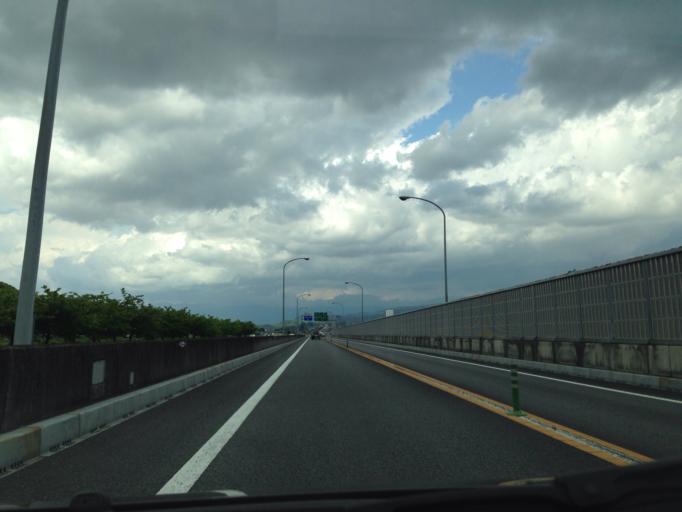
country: JP
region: Shizuoka
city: Mishima
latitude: 35.0040
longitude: 138.9366
